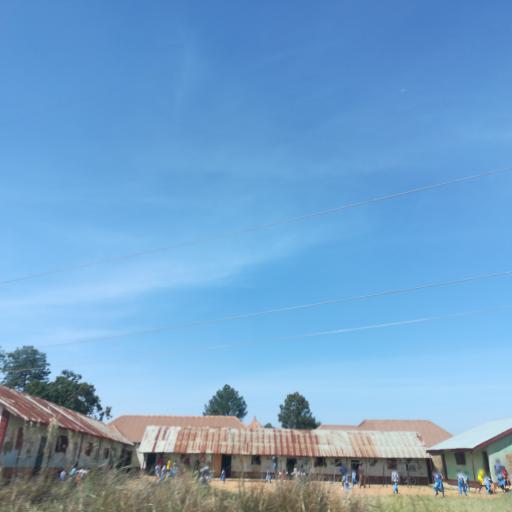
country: NG
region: Plateau
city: Bukuru
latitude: 9.7648
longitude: 8.8880
